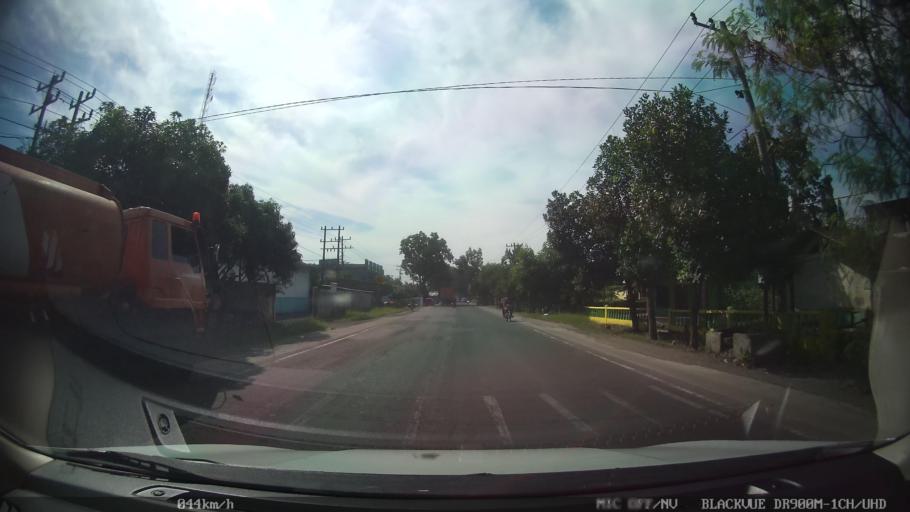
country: ID
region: North Sumatra
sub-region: Kabupaten Langkat
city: Stabat
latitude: 3.7285
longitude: 98.4958
